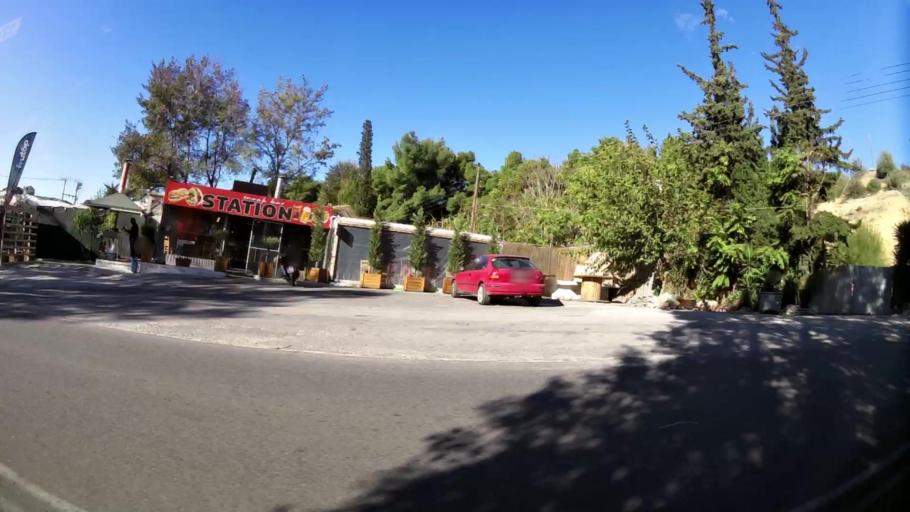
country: GR
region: Attica
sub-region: Nomarchia Athinas
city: Metamorfosi
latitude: 38.0772
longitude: 23.7614
